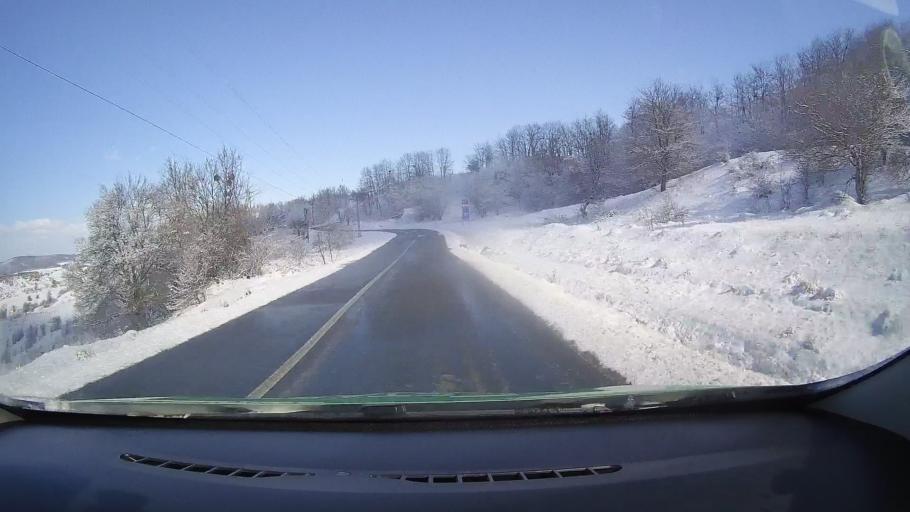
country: RO
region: Sibiu
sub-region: Comuna Rosia
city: Rosia
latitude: 45.7884
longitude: 24.3740
